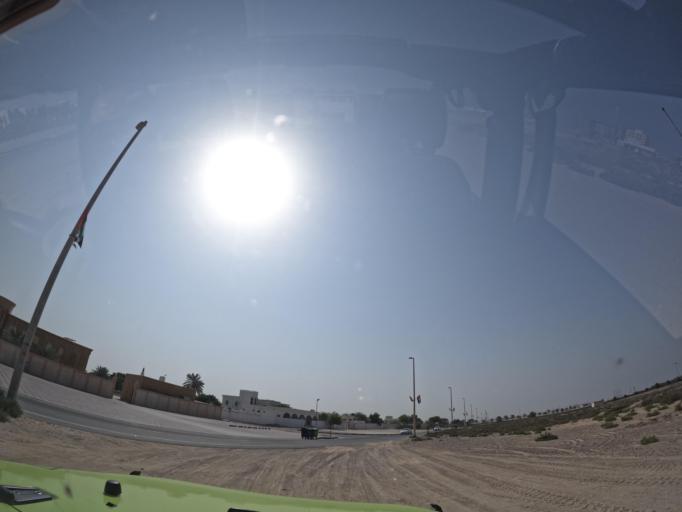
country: AE
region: Umm al Qaywayn
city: Umm al Qaywayn
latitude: 25.4784
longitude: 55.5308
